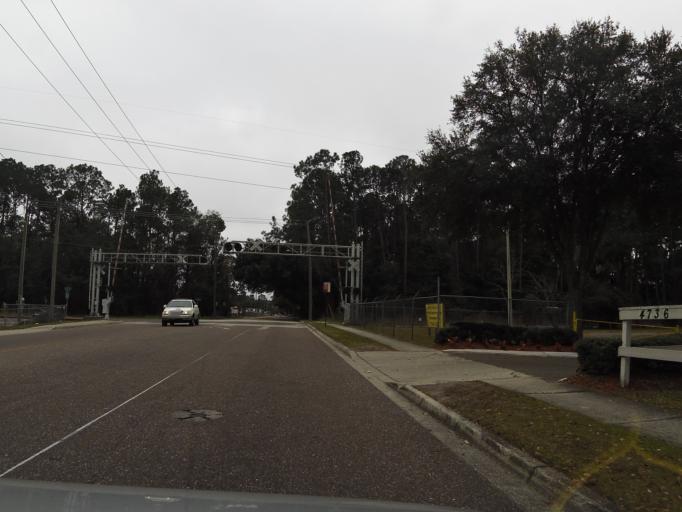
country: US
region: Florida
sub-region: Duval County
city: Jacksonville
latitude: 30.3652
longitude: -81.6989
